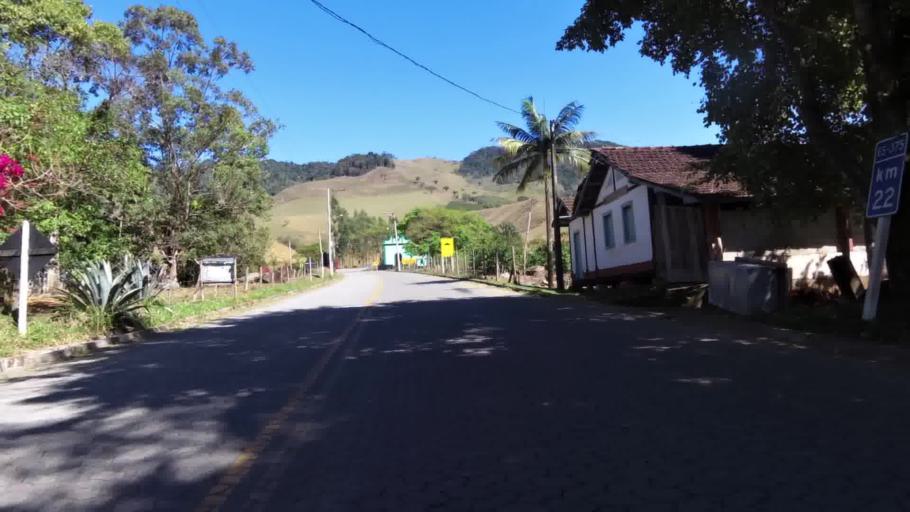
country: BR
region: Espirito Santo
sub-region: Vargem Alta
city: Vargem Alta
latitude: -20.7011
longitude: -40.9279
